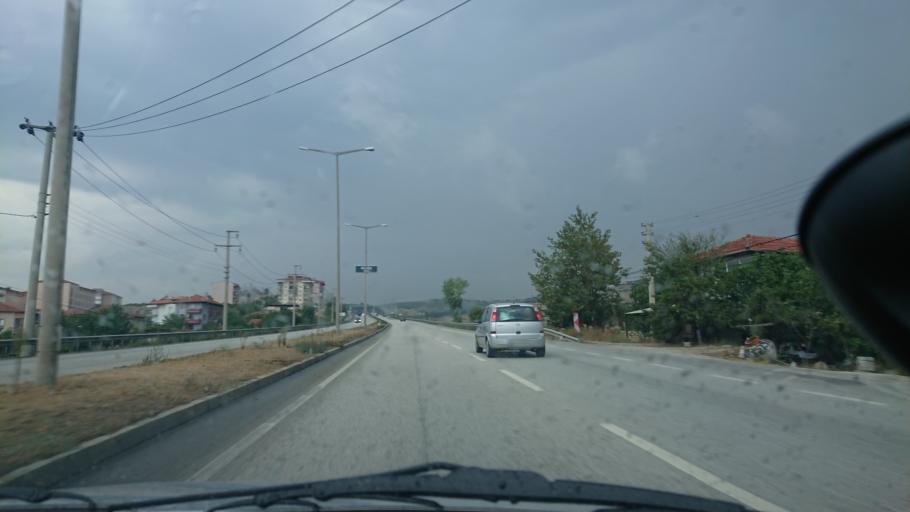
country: TR
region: Manisa
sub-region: Kula
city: Kula
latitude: 38.5447
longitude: 28.6266
